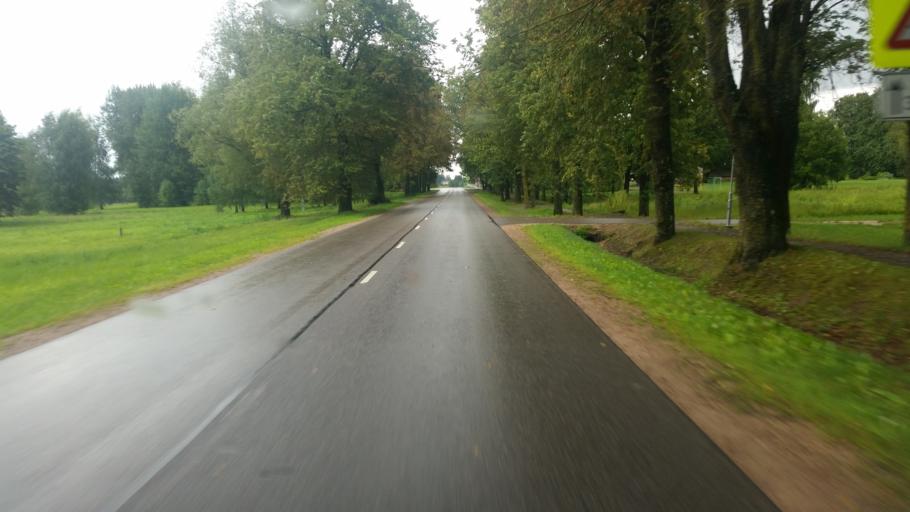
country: LV
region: Bauskas Rajons
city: Bauska
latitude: 56.4325
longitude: 24.3487
